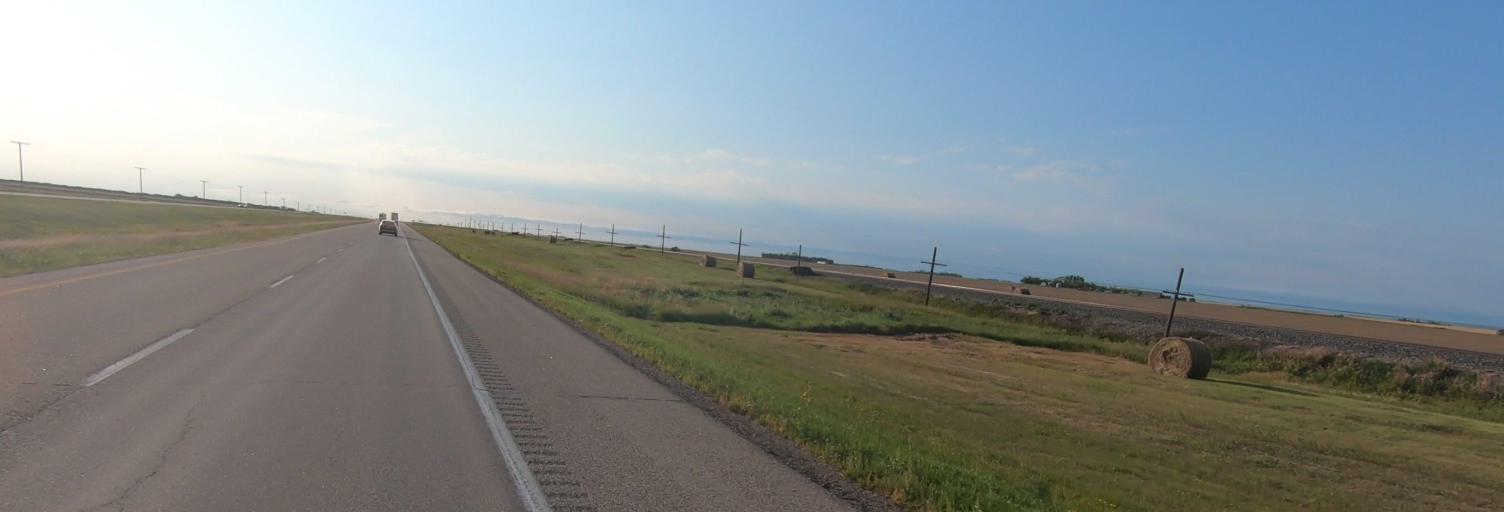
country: CA
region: Saskatchewan
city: Indian Head
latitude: 50.5058
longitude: -103.5339
